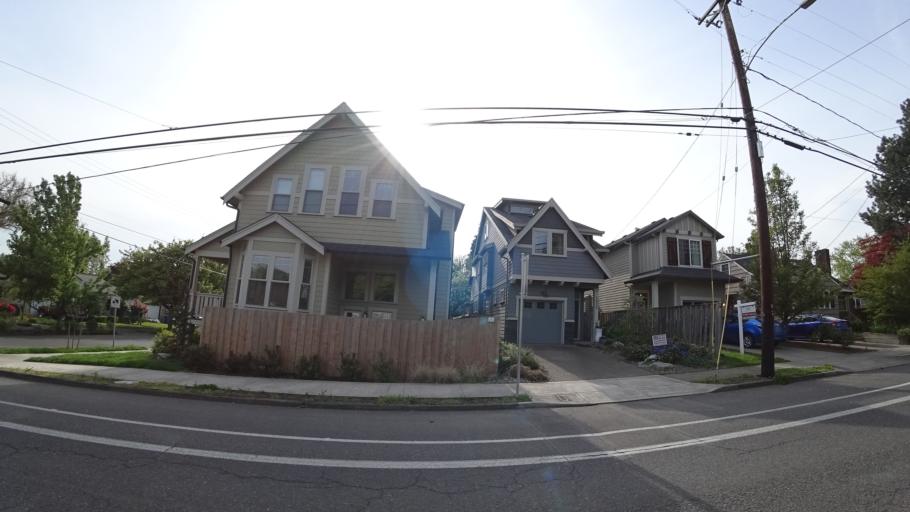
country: US
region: Oregon
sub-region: Clackamas County
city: Milwaukie
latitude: 45.4659
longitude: -122.6159
